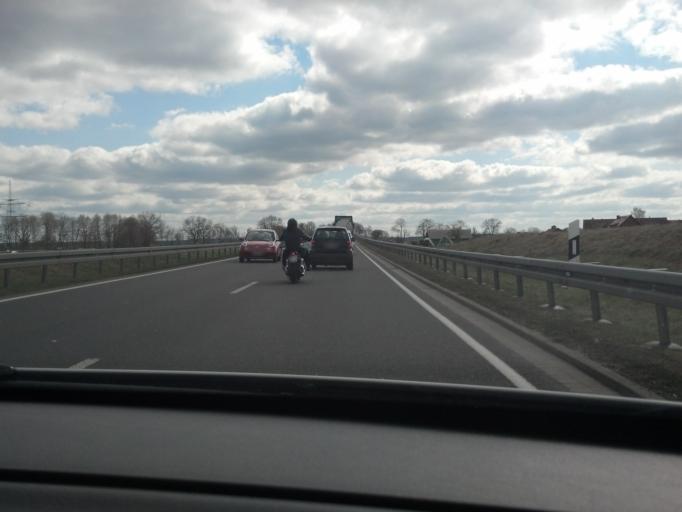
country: DE
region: Mecklenburg-Vorpommern
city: Neustrelitz
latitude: 53.3347
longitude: 13.1094
